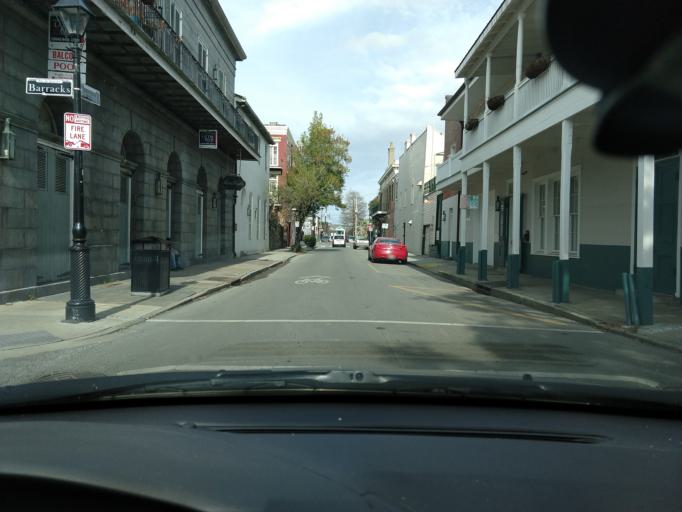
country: US
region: Louisiana
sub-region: Orleans Parish
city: New Orleans
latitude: 29.9646
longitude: -90.0632
